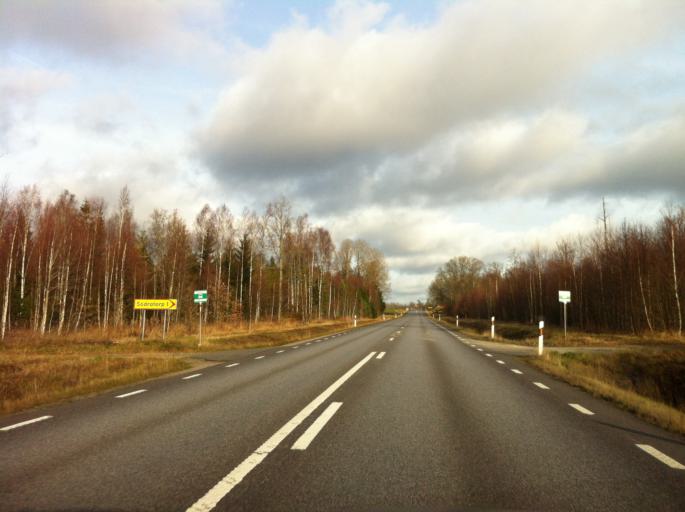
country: SE
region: Kronoberg
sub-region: Vaxjo Kommun
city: Gemla
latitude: 56.7818
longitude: 14.5990
